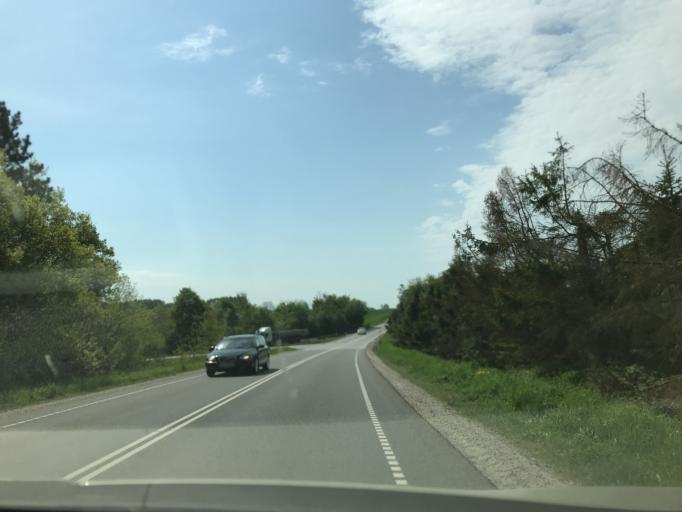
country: DK
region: South Denmark
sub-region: Middelfart Kommune
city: Ejby
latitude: 55.3858
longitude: 9.9175
